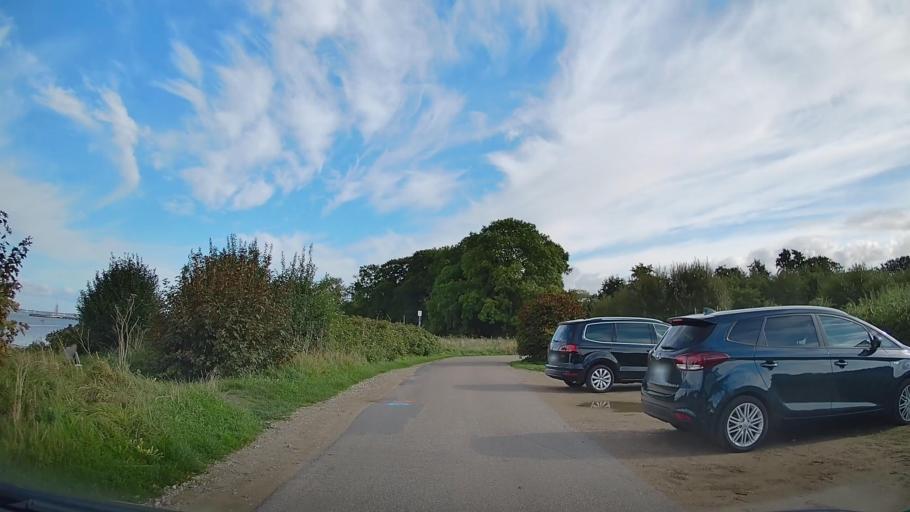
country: DE
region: Schleswig-Holstein
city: Ringsberg
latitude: 54.8302
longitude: 9.6047
